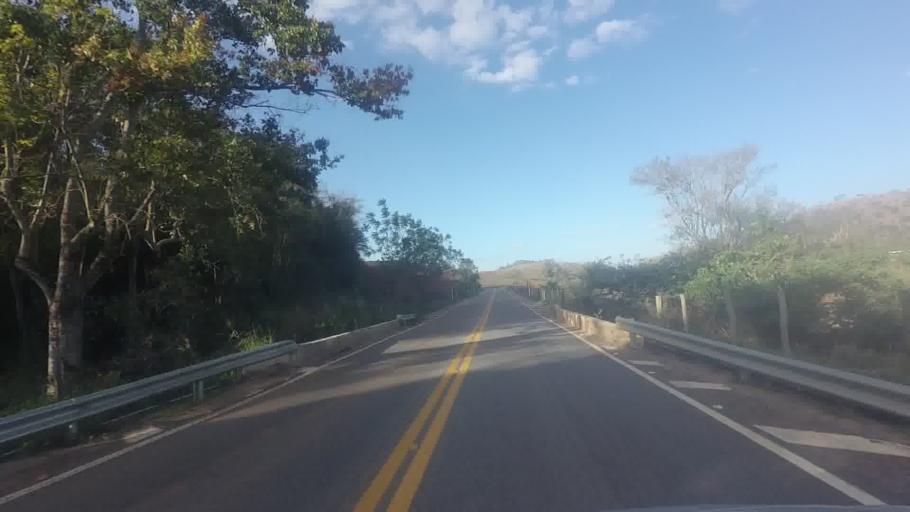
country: BR
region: Espirito Santo
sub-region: Jeronimo Monteiro
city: Jeronimo Monteiro
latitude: -20.9093
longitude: -41.2994
